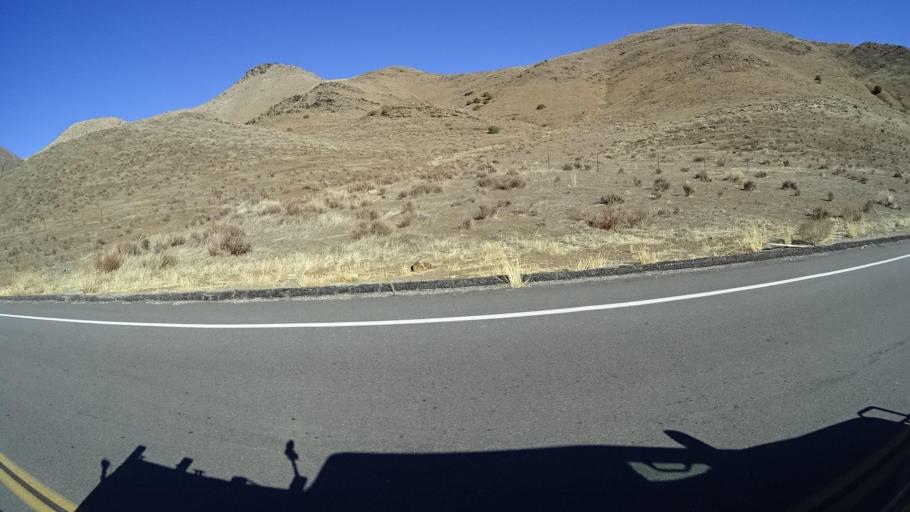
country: US
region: California
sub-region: Kern County
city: Wofford Heights
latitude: 35.6799
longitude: -118.4074
